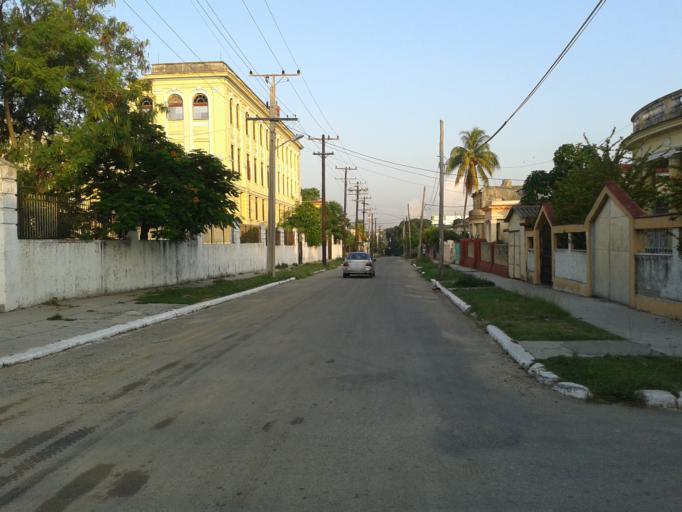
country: CU
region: La Habana
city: Diez de Octubre
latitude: 23.0932
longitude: -82.3686
